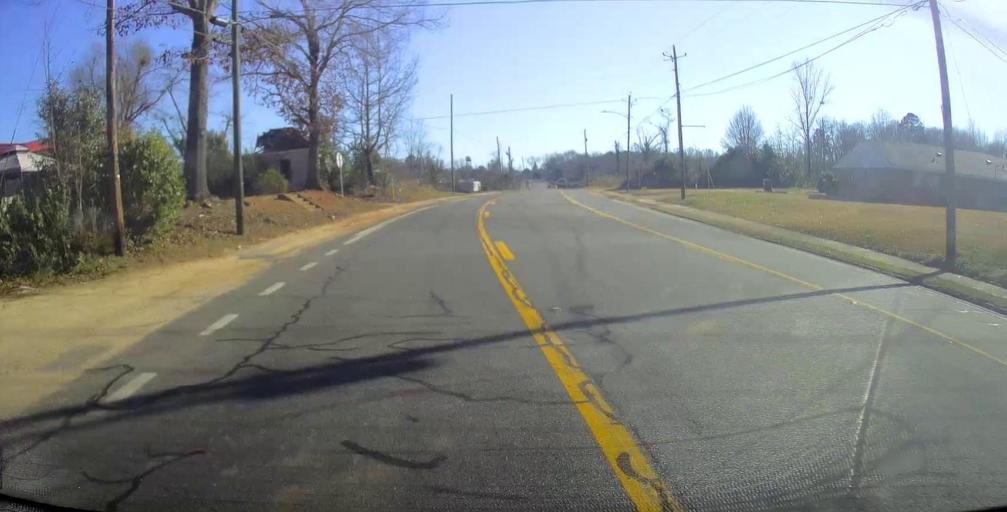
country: US
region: Georgia
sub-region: Talbot County
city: Talbotton
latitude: 32.6872
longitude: -84.5398
